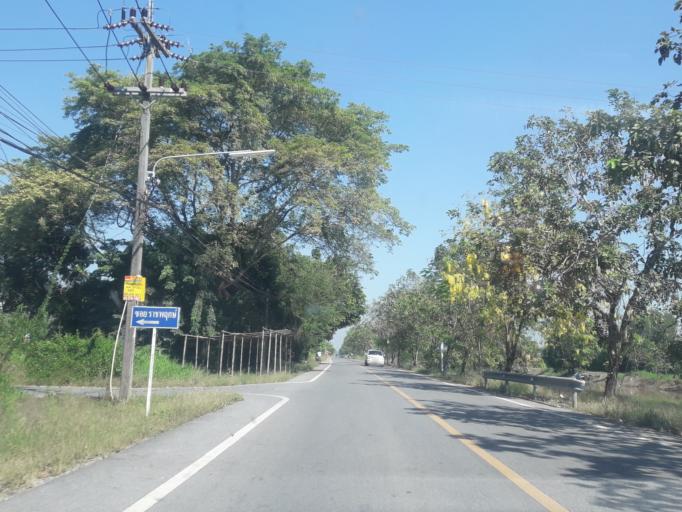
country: TH
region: Pathum Thani
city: Nong Suea
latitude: 14.1484
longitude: 100.8459
